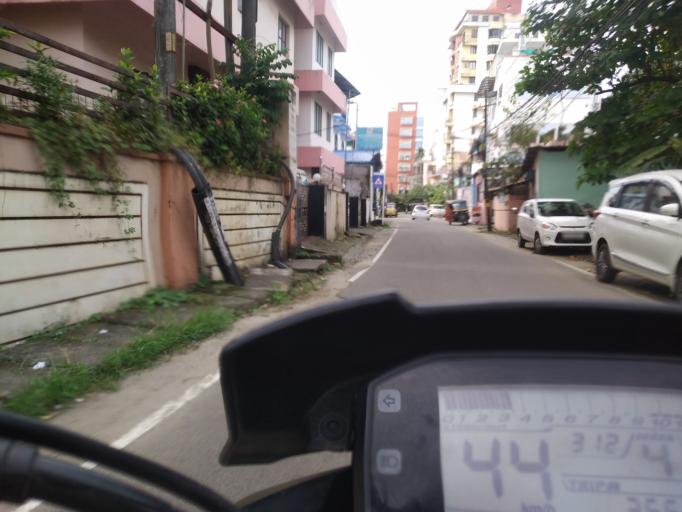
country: IN
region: Kerala
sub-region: Ernakulam
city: Cochin
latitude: 9.9702
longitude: 76.2887
